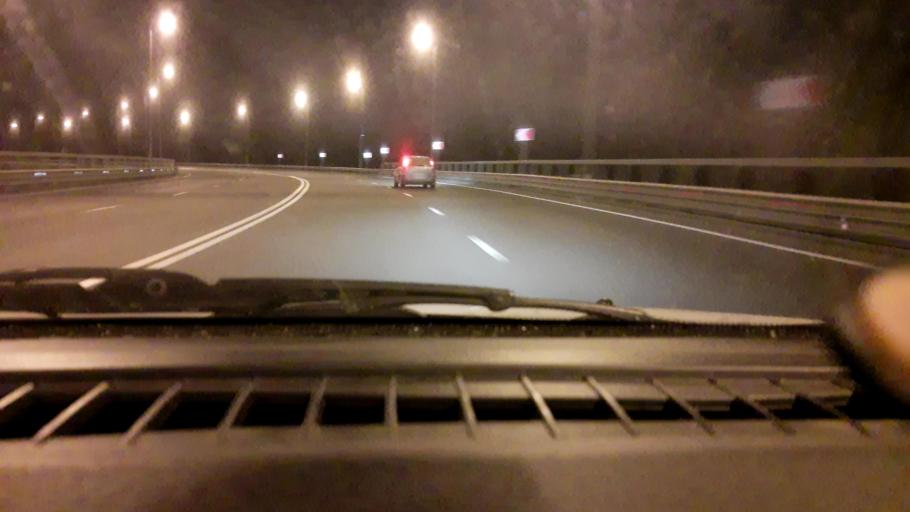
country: RU
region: Nizjnij Novgorod
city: Gorbatovka
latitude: 56.2280
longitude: 43.8036
